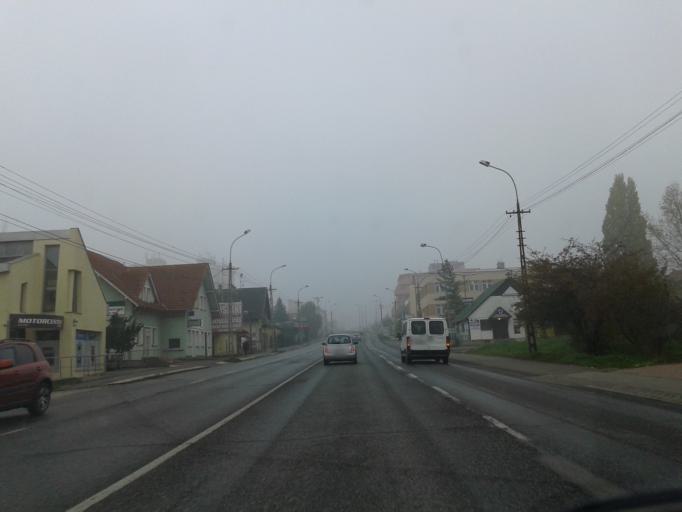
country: HU
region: Pest
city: Erd
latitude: 47.3787
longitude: 18.9301
